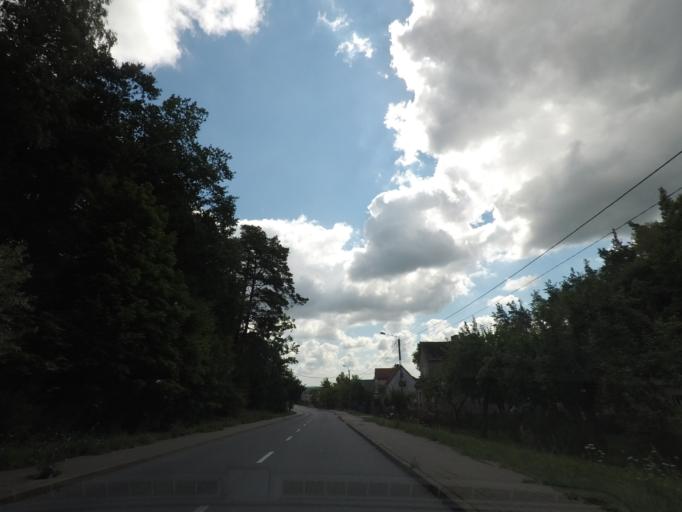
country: PL
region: Pomeranian Voivodeship
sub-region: Powiat wejherowski
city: Leczyce
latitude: 54.5951
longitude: 17.8532
